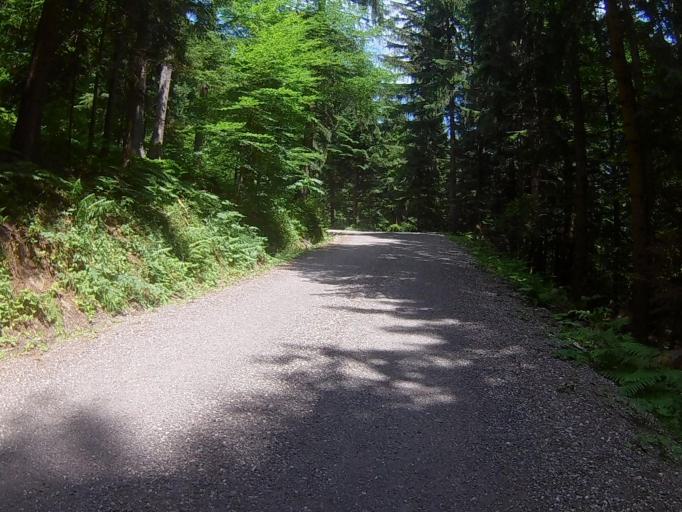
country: SI
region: Maribor
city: Pekre
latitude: 46.4997
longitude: 15.5652
